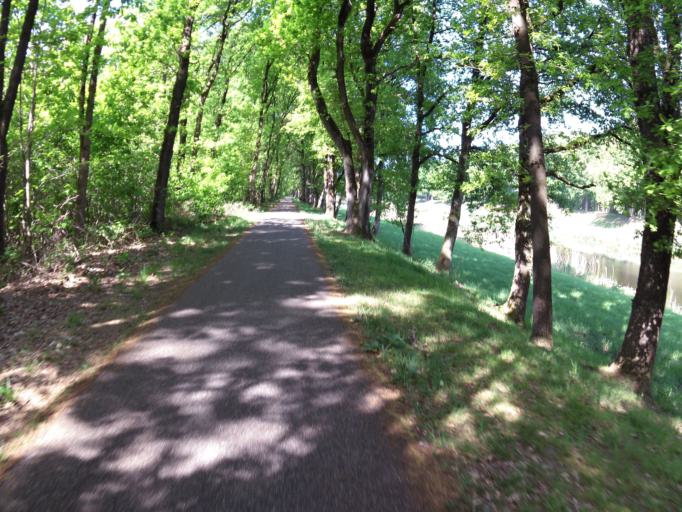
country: NL
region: North Brabant
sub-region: Gemeente Heusden
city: Heusden
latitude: 51.6686
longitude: 5.1369
